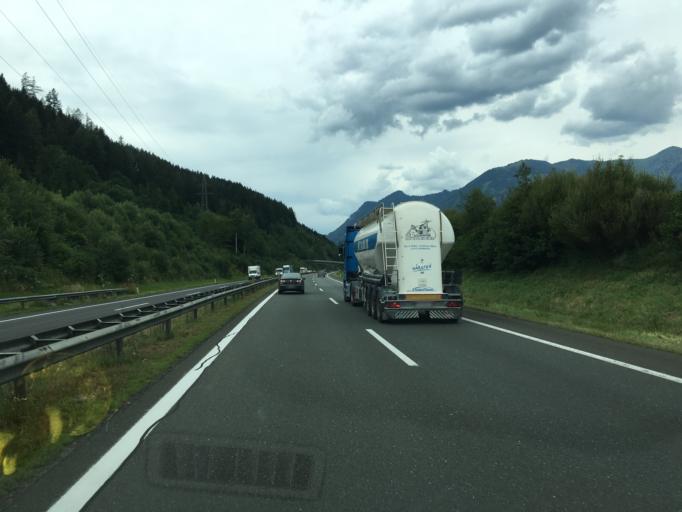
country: AT
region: Styria
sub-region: Politischer Bezirk Leoben
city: Traboch
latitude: 47.3762
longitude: 14.9560
